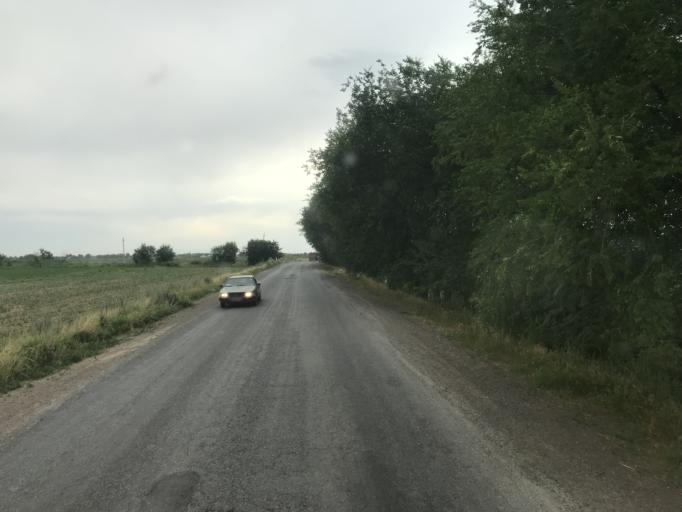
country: KZ
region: Ongtustik Qazaqstan
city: Asykata
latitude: 40.9513
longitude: 68.4465
